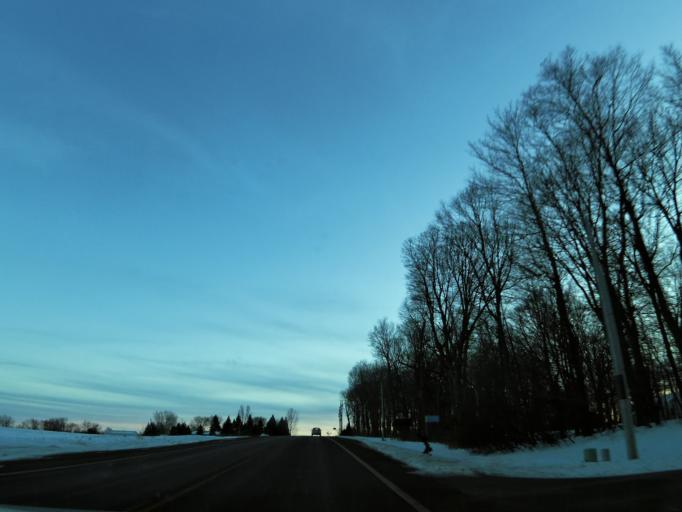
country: US
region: Minnesota
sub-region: Carver County
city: Chaska
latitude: 44.7563
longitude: -93.5614
